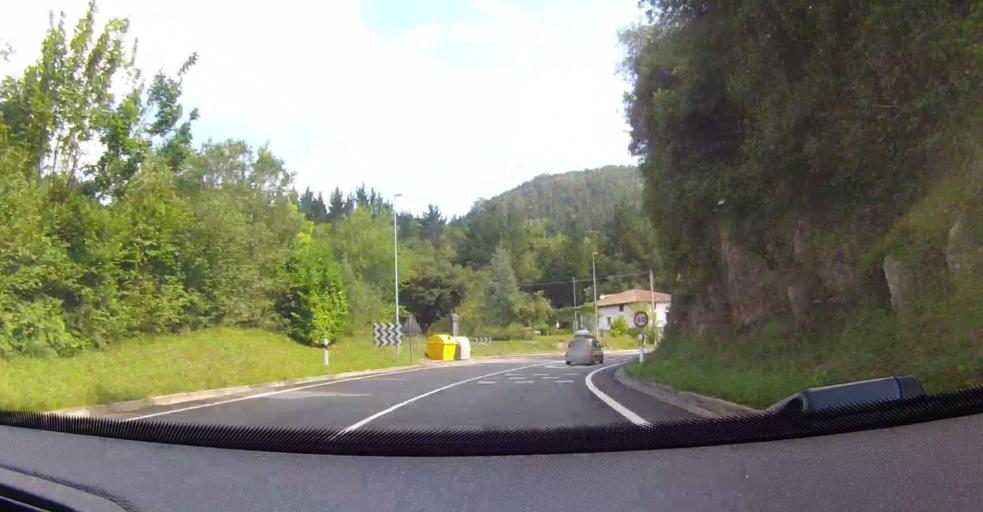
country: ES
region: Basque Country
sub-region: Bizkaia
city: Kortezubi
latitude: 43.3601
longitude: -2.6381
